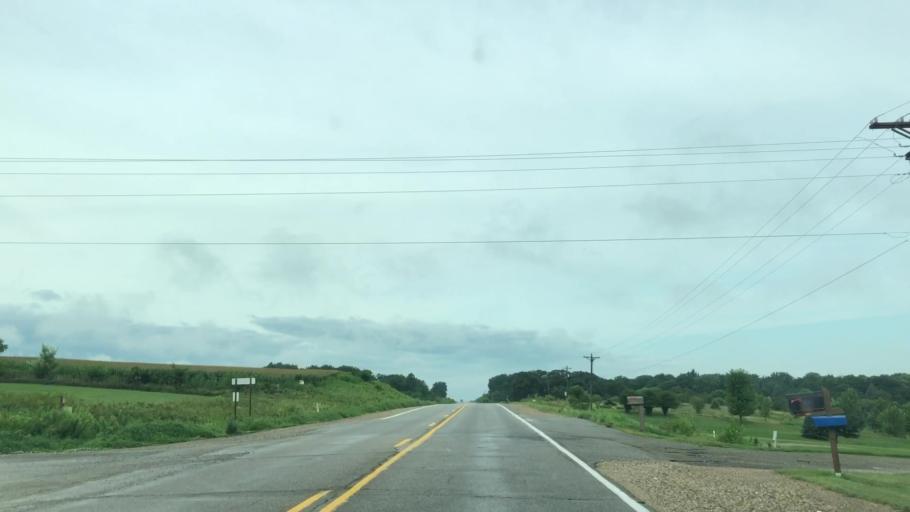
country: US
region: Iowa
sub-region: Marshall County
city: Marshalltown
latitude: 42.0075
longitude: -92.9413
